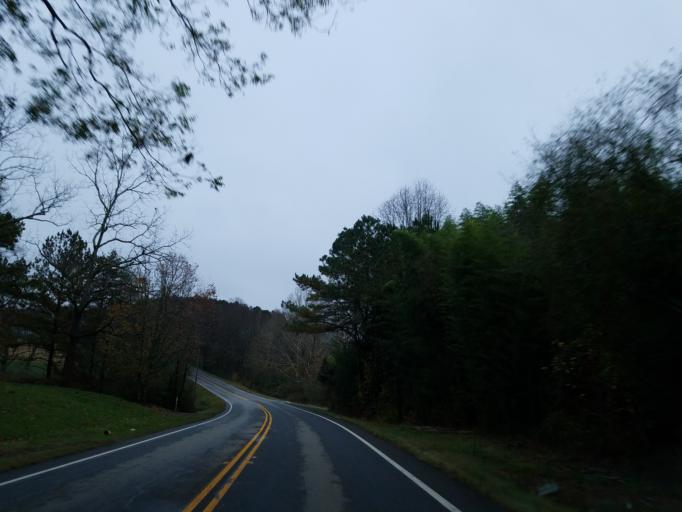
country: US
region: Georgia
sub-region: Pickens County
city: Nelson
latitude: 34.3899
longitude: -84.4356
